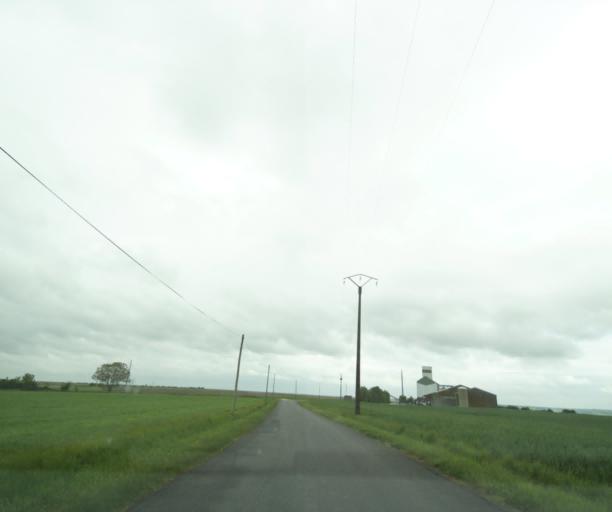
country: FR
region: Poitou-Charentes
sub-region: Departement de la Charente-Maritime
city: Perignac
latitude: 45.6584
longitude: -0.5049
